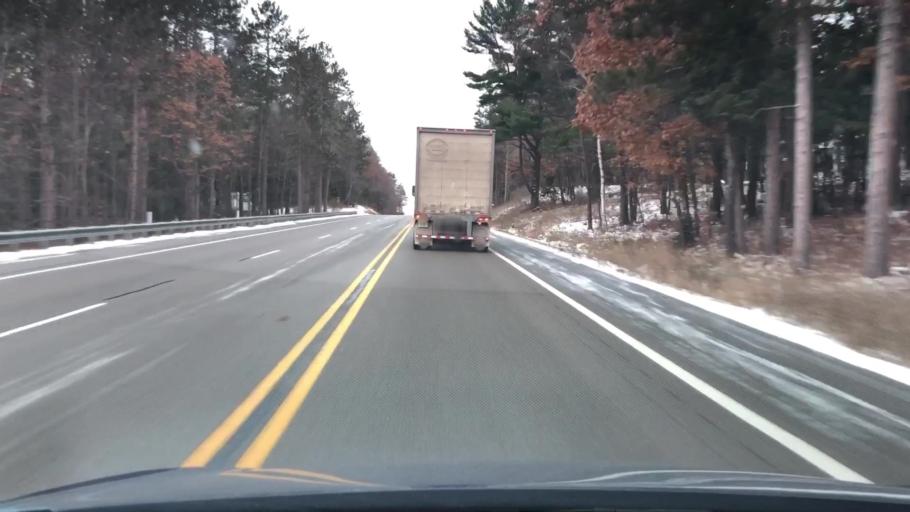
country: US
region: Michigan
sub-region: Wexford County
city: Cadillac
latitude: 44.1857
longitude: -85.3873
